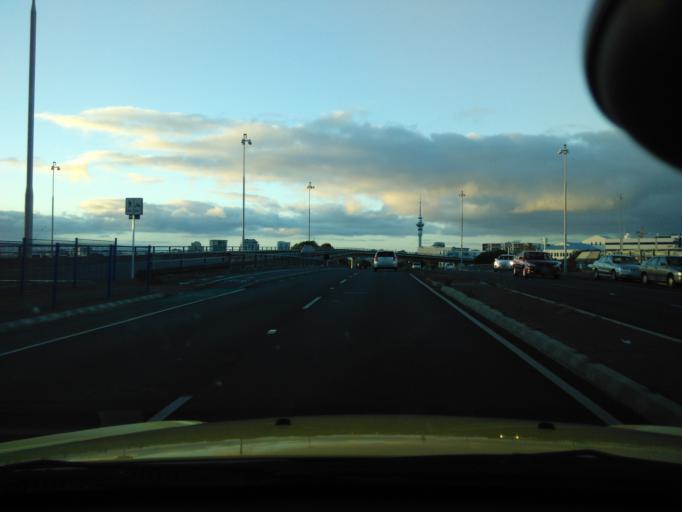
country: NZ
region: Auckland
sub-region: Auckland
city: Auckland
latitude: -36.8697
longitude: 174.7530
